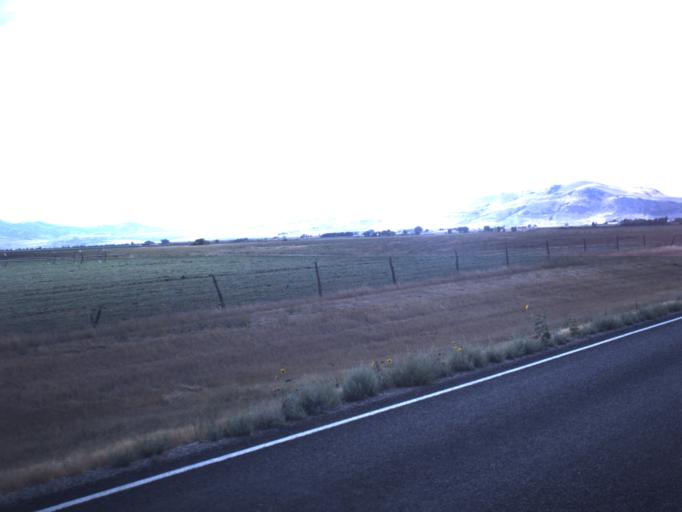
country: US
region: Utah
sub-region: Cache County
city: Lewiston
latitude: 41.9249
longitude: -111.8741
